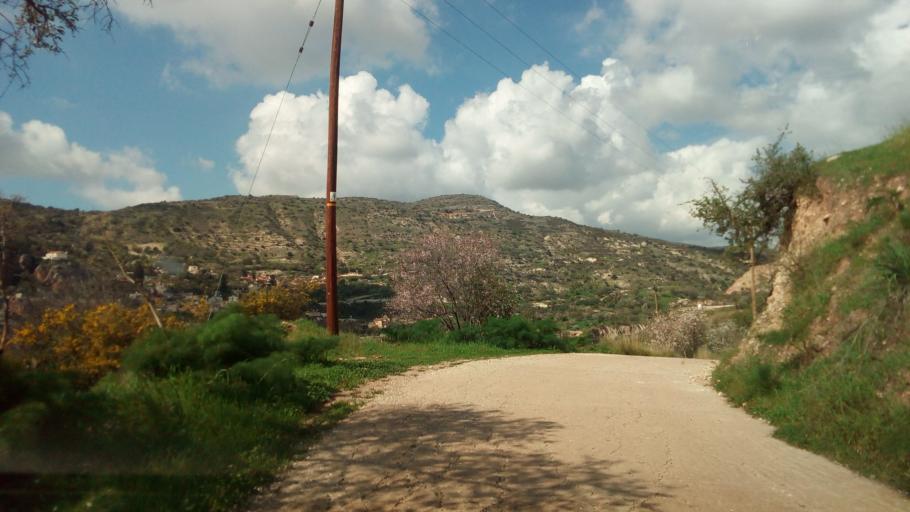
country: CY
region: Pafos
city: Mesogi
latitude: 34.7941
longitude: 32.5335
